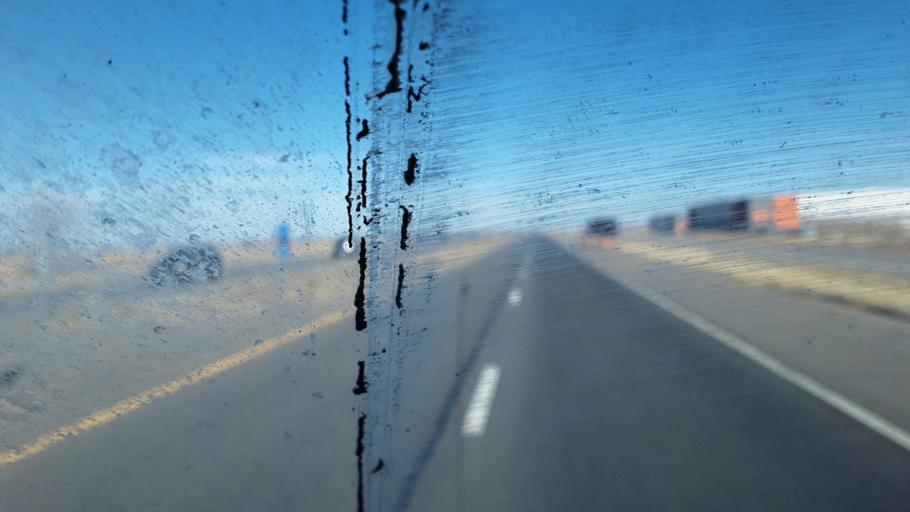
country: US
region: Colorado
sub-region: Weld County
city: Lochbuie
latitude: 39.9930
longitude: -104.7270
